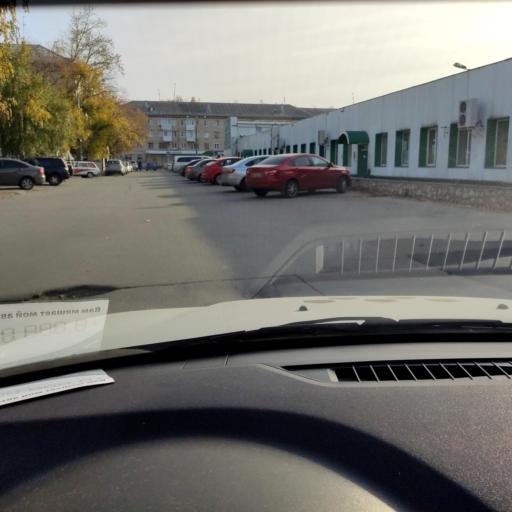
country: RU
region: Samara
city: Tol'yatti
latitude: 53.5079
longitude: 49.4038
